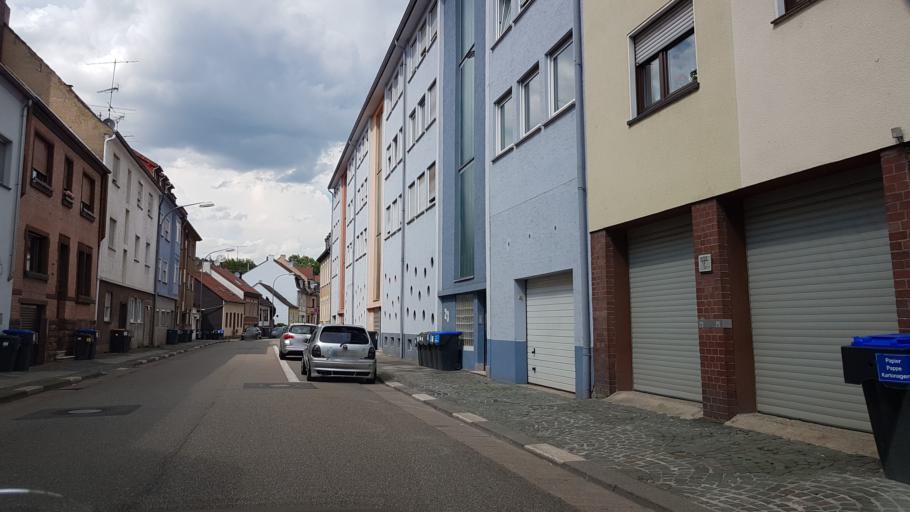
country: DE
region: Saarland
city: Saarbrucken
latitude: 49.2560
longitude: 6.9752
